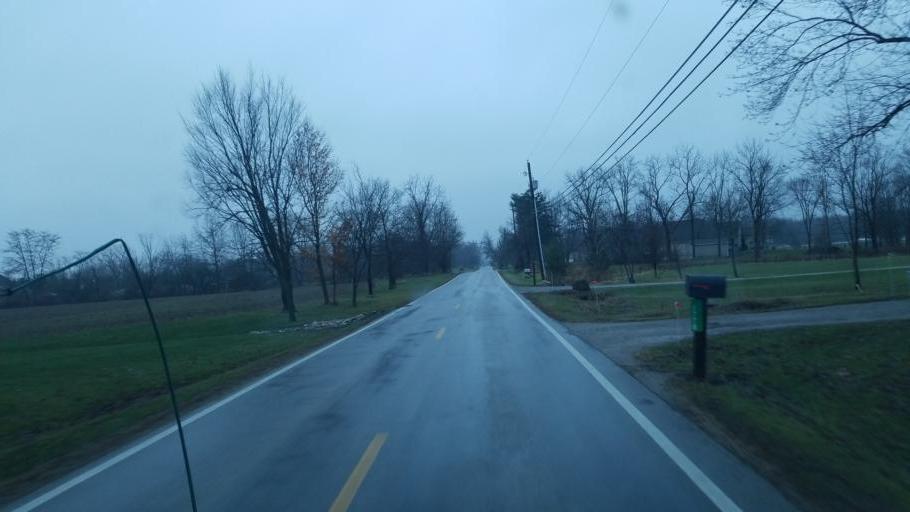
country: US
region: Ohio
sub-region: Delaware County
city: Delaware
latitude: 40.2628
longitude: -83.0433
